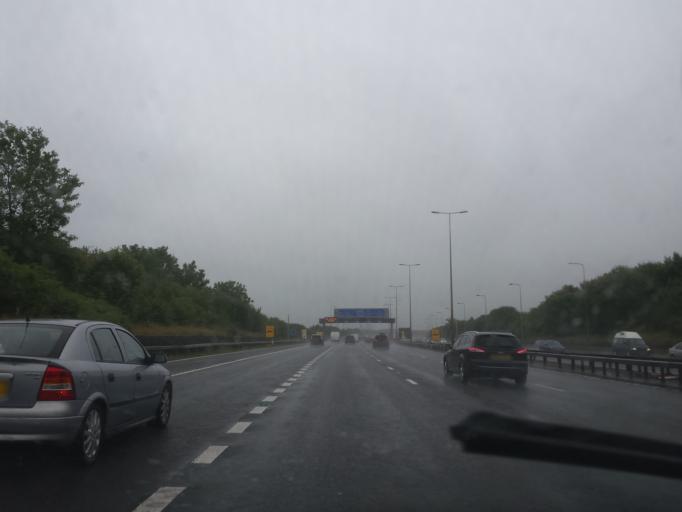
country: GB
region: England
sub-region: Leicestershire
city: Enderby
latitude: 52.6091
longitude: -1.1983
